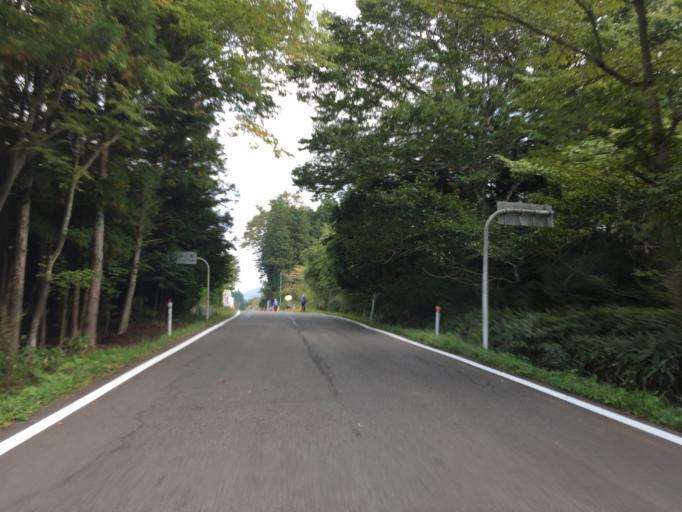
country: JP
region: Fukushima
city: Funehikimachi-funehiki
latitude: 37.5823
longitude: 140.7194
